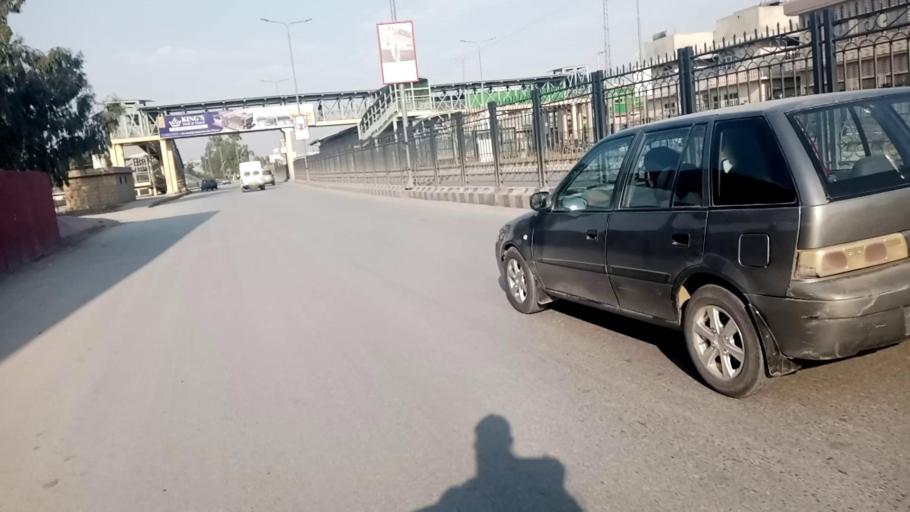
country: PK
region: Khyber Pakhtunkhwa
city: Peshawar
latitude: 33.9897
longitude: 71.4542
